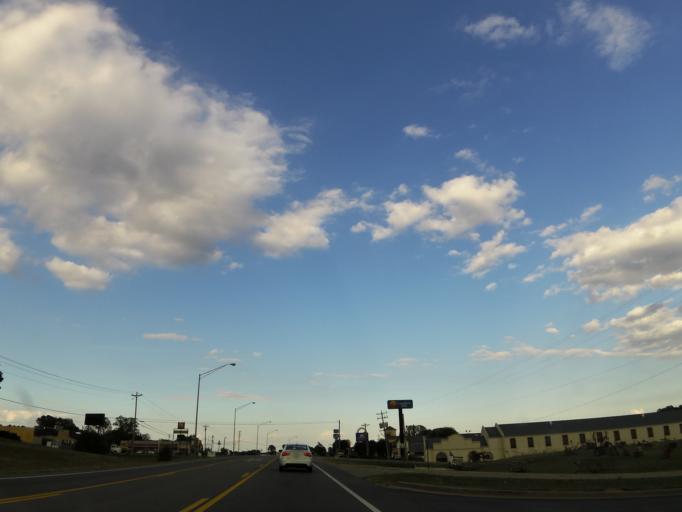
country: US
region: Tennessee
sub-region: Maury County
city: Spring Hill
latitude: 35.6430
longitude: -86.9004
